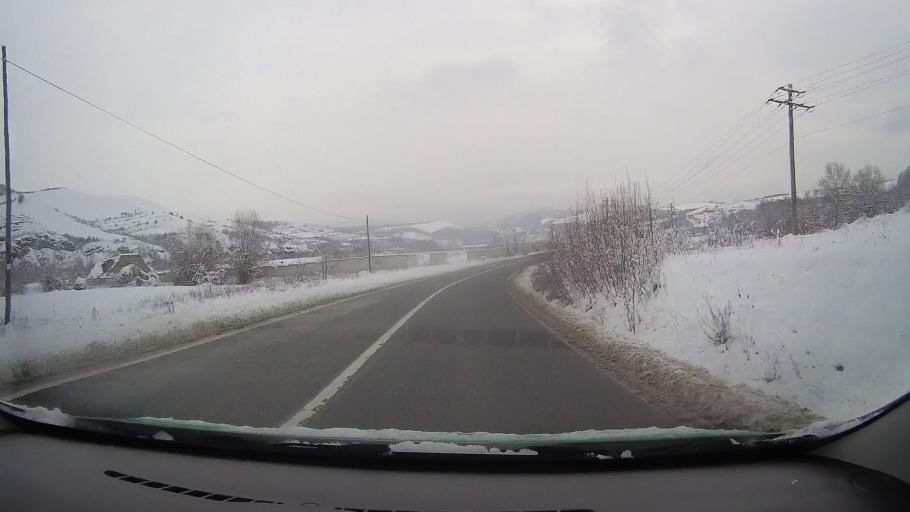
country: RO
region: Alba
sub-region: Comuna Sasciori
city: Sebesel
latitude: 45.8992
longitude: 23.5597
